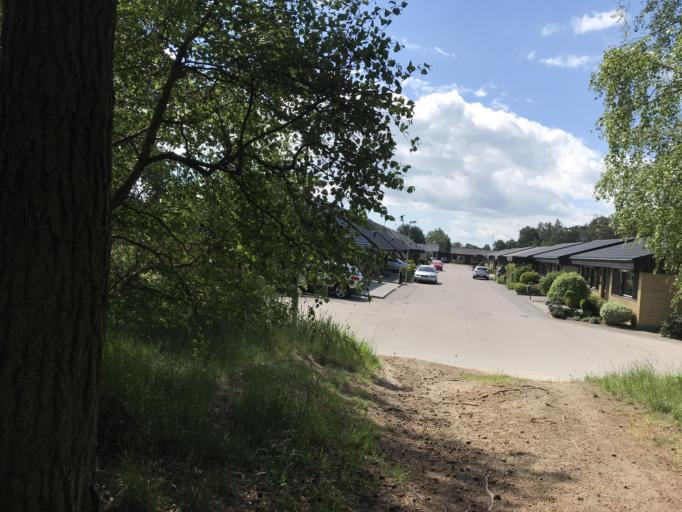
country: SE
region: Skane
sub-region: Landskrona
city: Asmundtorp
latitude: 55.8513
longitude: 12.9164
